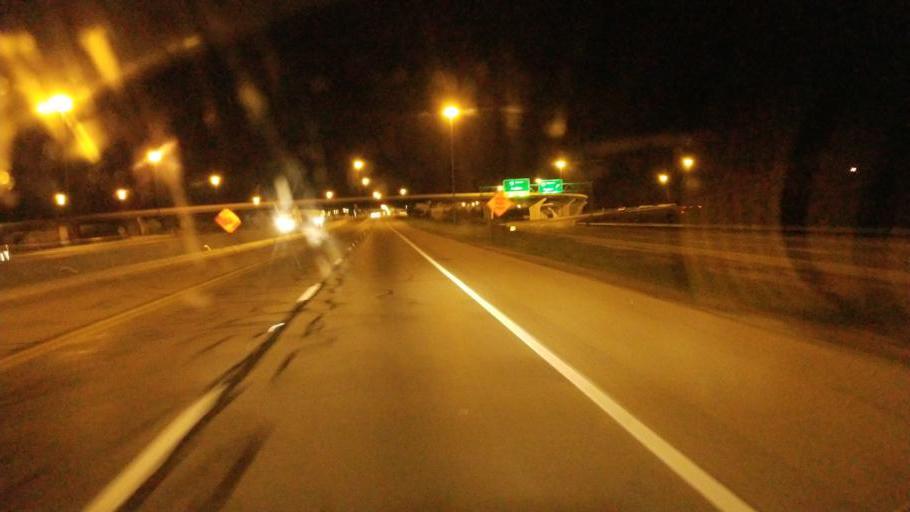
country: US
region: Ohio
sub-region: Montgomery County
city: Vandalia
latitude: 39.8659
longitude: -84.1831
